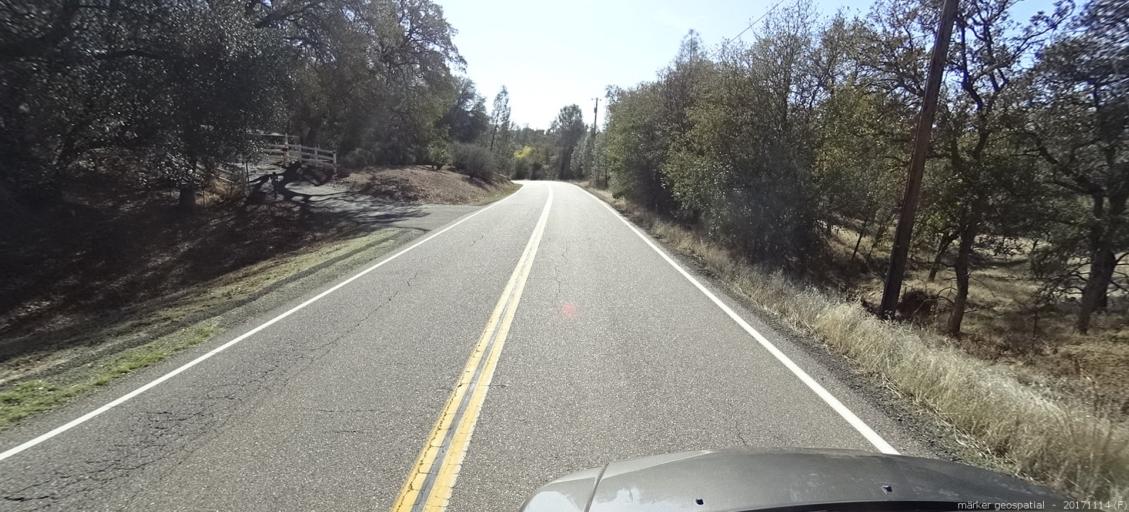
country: US
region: California
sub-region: Shasta County
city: Anderson
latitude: 40.4038
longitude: -122.3548
